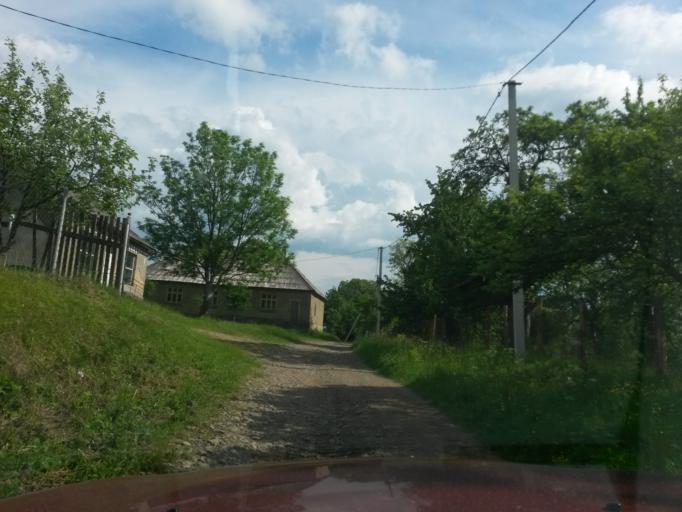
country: UA
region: Zakarpattia
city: Velykyi Bereznyi
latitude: 48.8994
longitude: 22.5275
